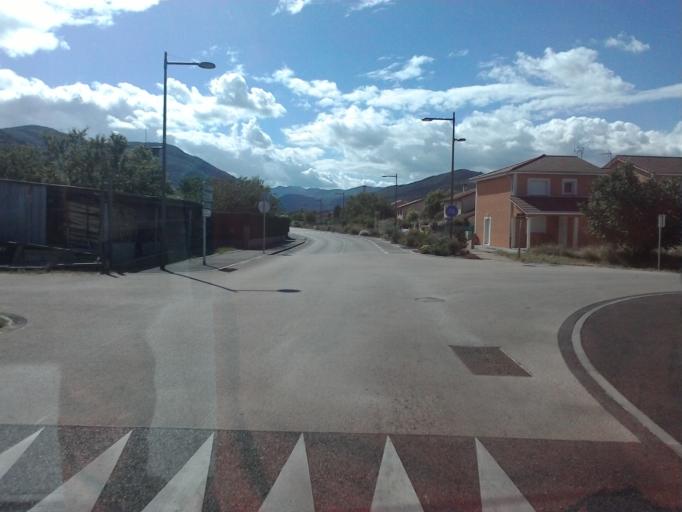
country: FR
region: Rhone-Alpes
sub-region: Departement de l'Ain
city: Amberieu-en-Bugey
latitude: 45.9544
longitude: 5.3555
